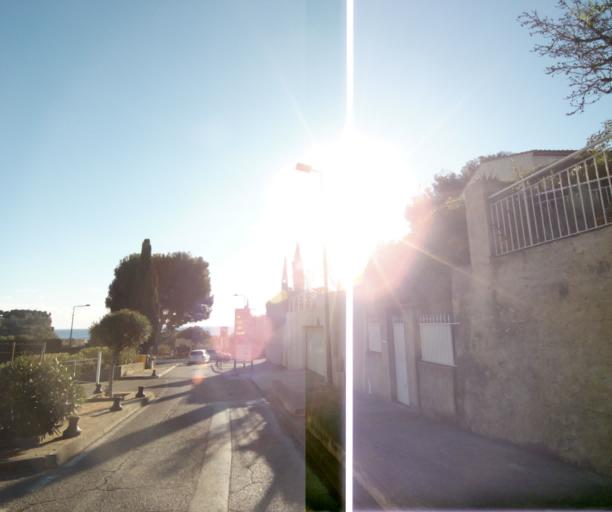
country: FR
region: Provence-Alpes-Cote d'Azur
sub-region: Departement des Bouches-du-Rhone
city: Cassis
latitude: 43.2188
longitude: 5.5397
